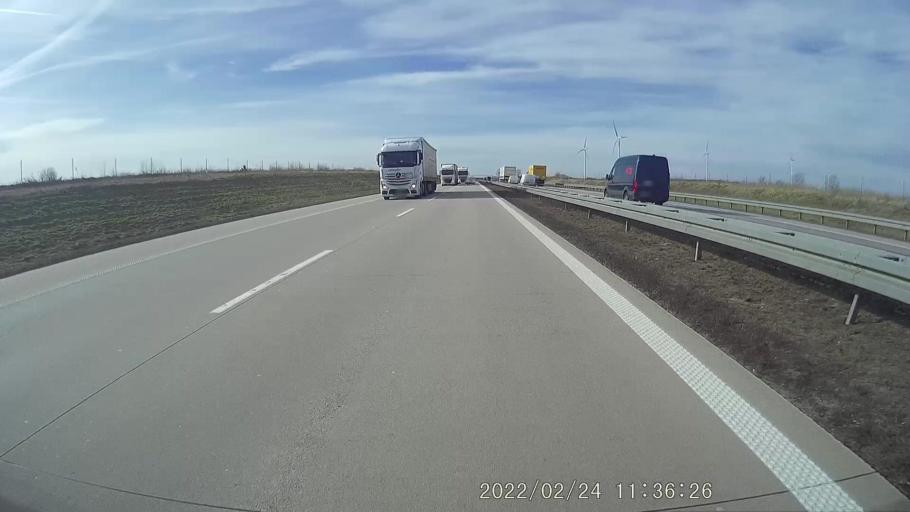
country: PL
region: Lower Silesian Voivodeship
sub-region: Powiat polkowicki
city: Przemkow
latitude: 51.5224
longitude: 15.8066
